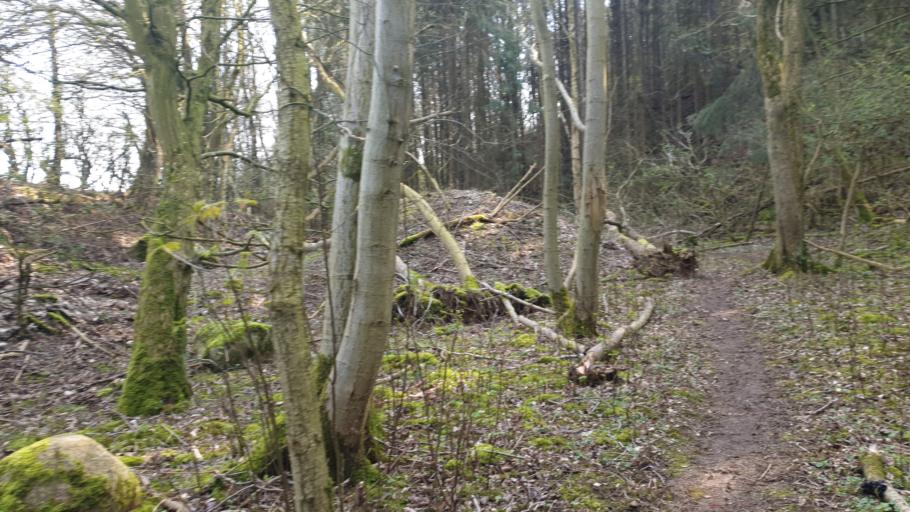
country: DK
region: Central Jutland
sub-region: Hedensted Kommune
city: Hedensted
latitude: 55.8103
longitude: 9.6941
